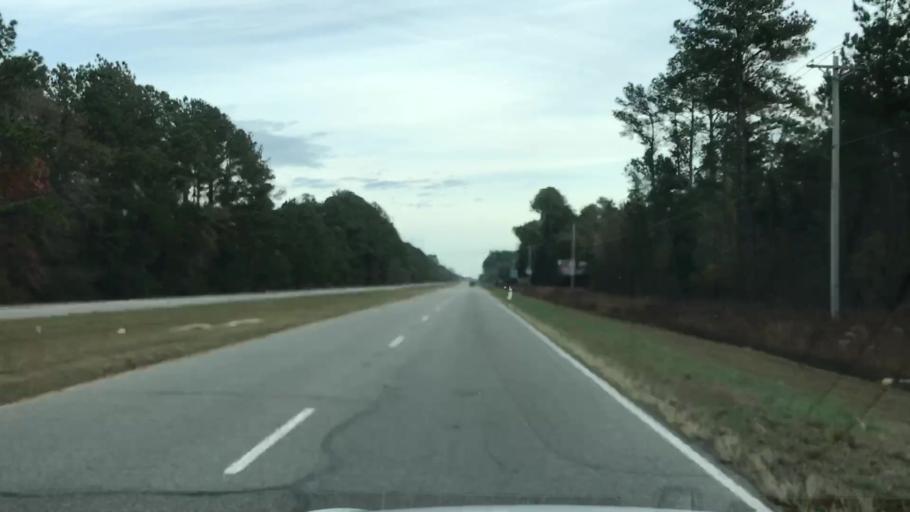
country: US
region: South Carolina
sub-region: Georgetown County
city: Georgetown
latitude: 33.3064
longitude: -79.3354
